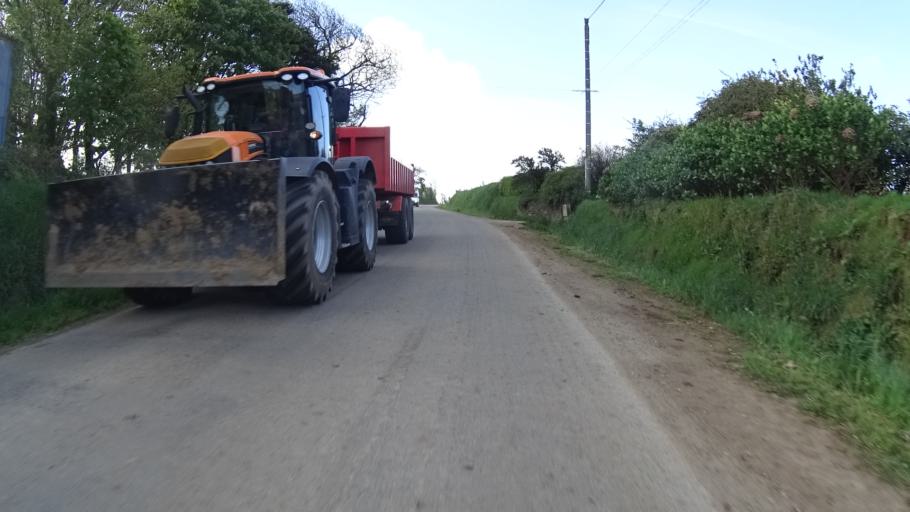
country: FR
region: Brittany
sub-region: Departement du Finistere
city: Plouzane
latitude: 48.3961
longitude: -4.6651
